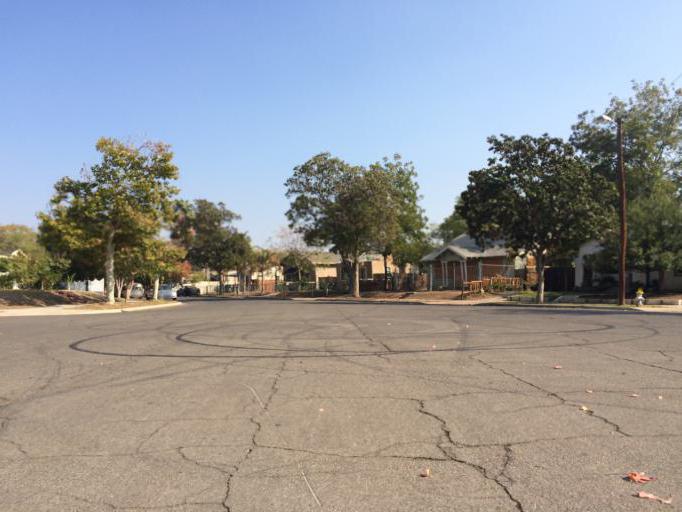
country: US
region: California
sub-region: Fresno County
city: Fresno
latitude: 36.7468
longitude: -119.7525
